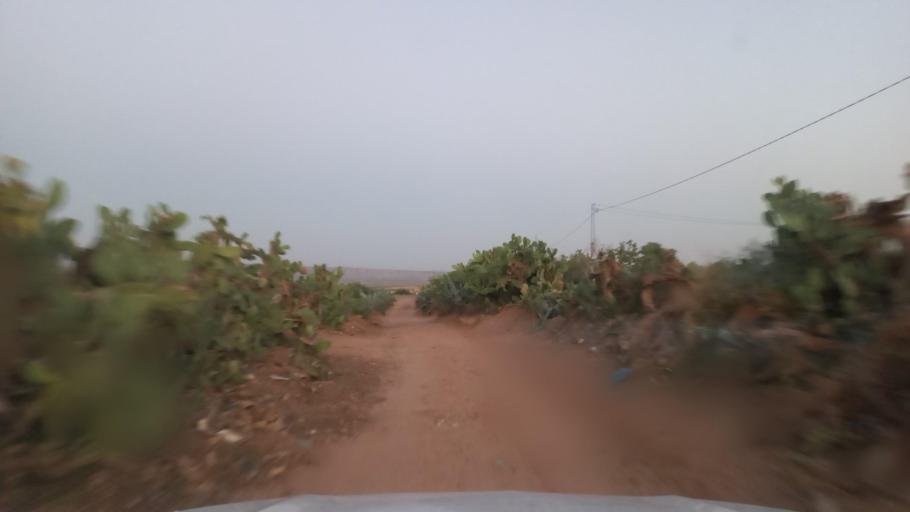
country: TN
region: Al Qasrayn
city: Sbiba
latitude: 35.3770
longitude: 9.0157
